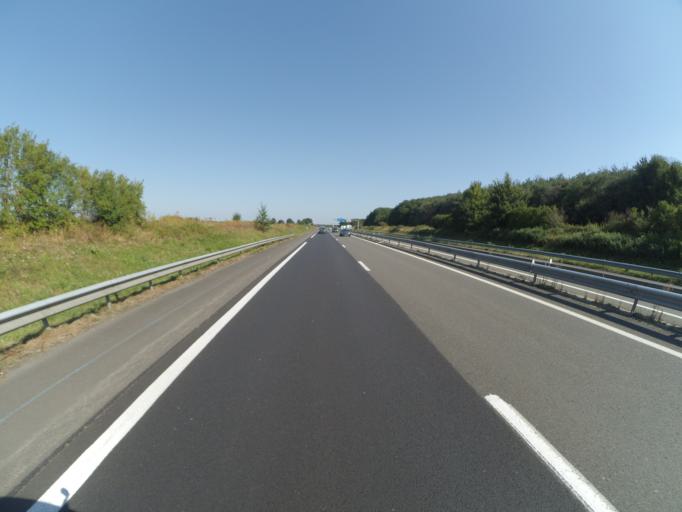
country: FR
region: Pays de la Loire
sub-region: Departement de la Vendee
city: Bouffere
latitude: 46.9566
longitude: -1.3563
